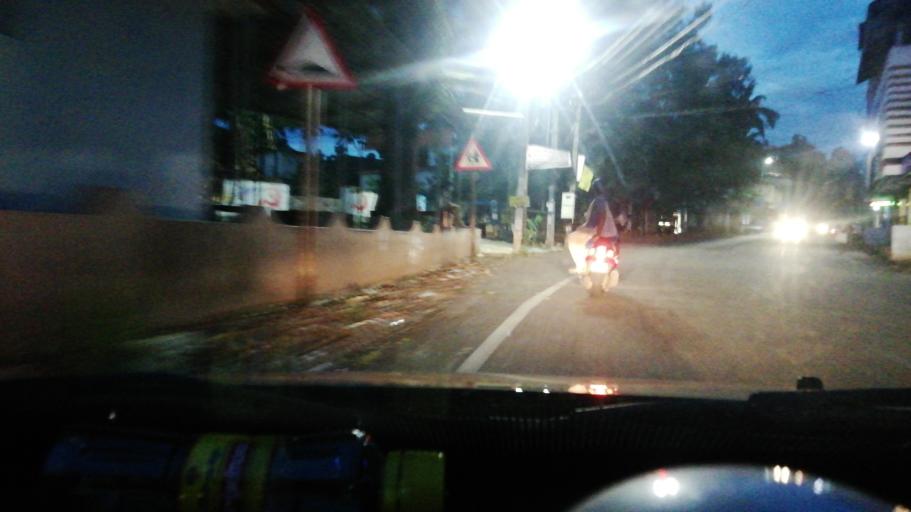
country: IN
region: Kerala
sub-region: Thiruvananthapuram
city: Paravur
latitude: 8.8126
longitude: 76.6793
